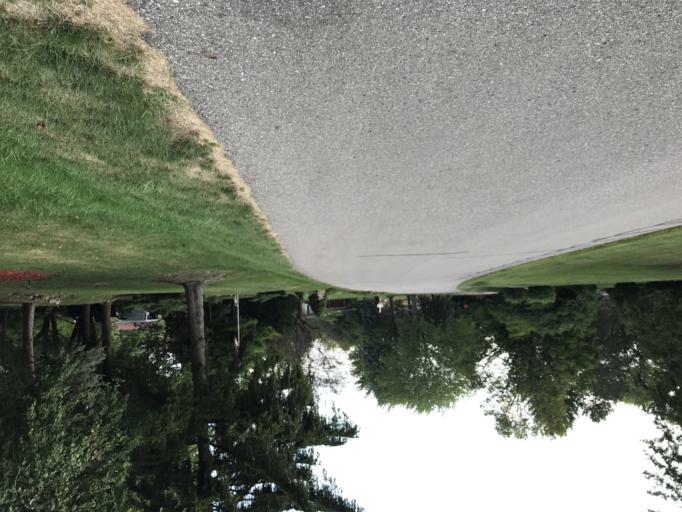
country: US
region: Michigan
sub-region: Oakland County
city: Farmington Hills
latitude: 42.4859
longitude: -83.3531
